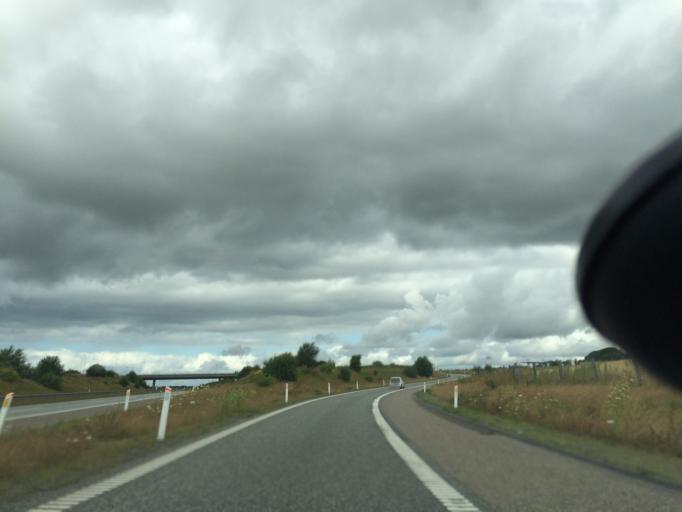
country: DK
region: Central Jutland
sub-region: Skanderborg Kommune
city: Galten
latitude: 56.1444
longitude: 9.9227
